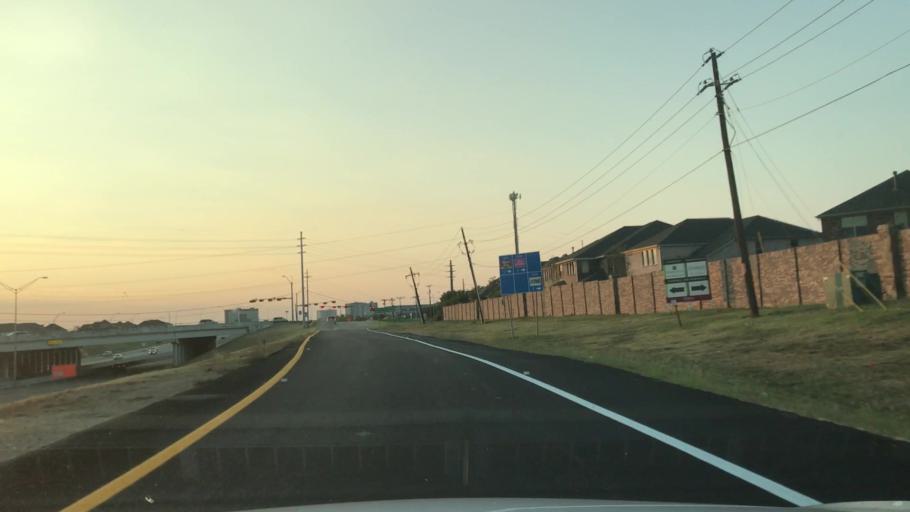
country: US
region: Texas
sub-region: Dallas County
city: Coppell
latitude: 32.9051
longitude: -96.9908
